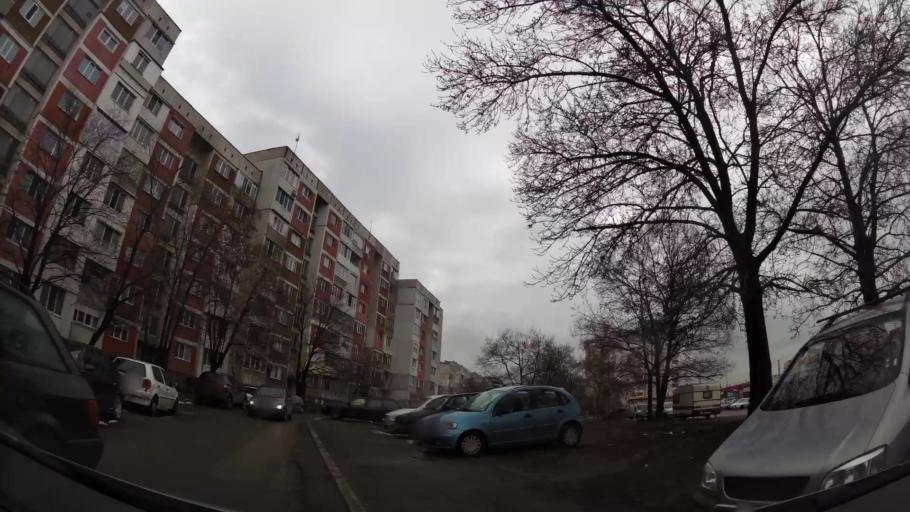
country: BG
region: Sofiya
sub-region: Obshtina Bozhurishte
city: Bozhurishte
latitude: 42.7307
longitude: 23.2487
